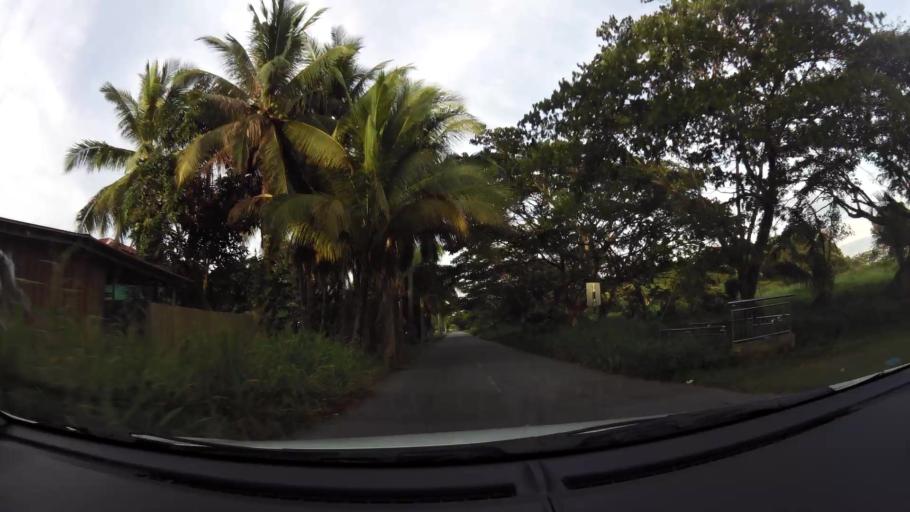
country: BN
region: Brunei and Muara
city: Bandar Seri Begawan
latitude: 4.9294
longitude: 114.8875
